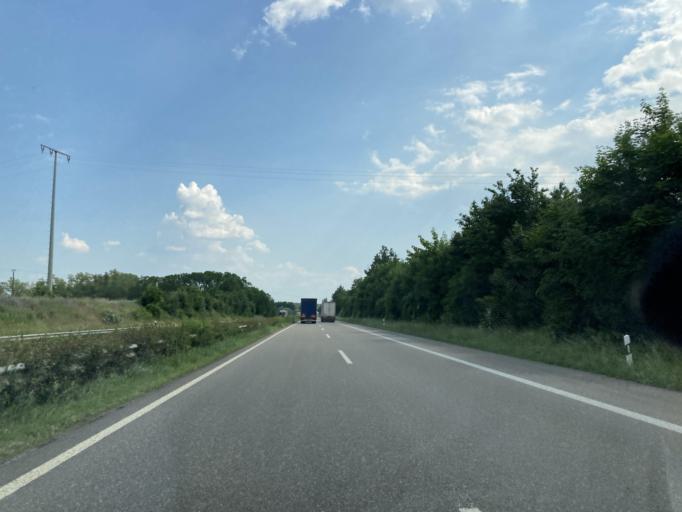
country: DE
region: Rheinland-Pfalz
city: Kuhardt
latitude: 49.1424
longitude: 8.3049
